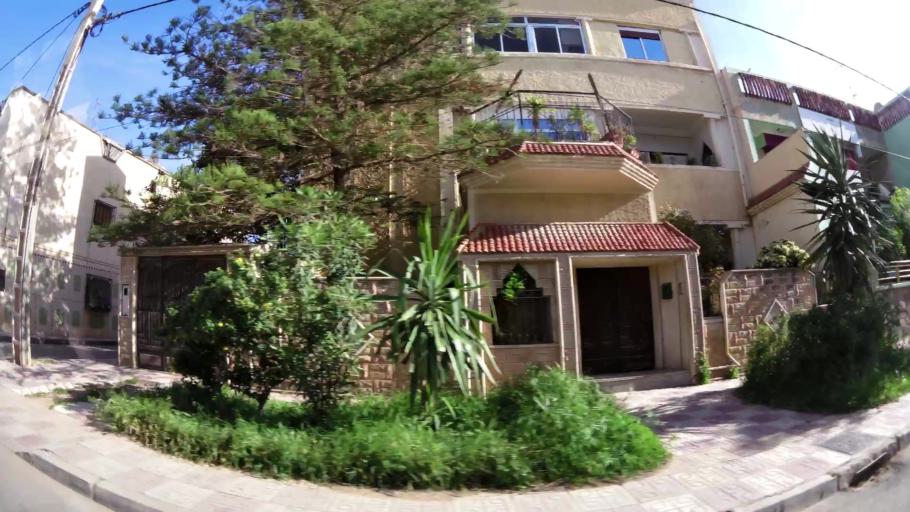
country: MA
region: Oriental
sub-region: Oujda-Angad
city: Oujda
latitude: 34.6751
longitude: -1.9066
